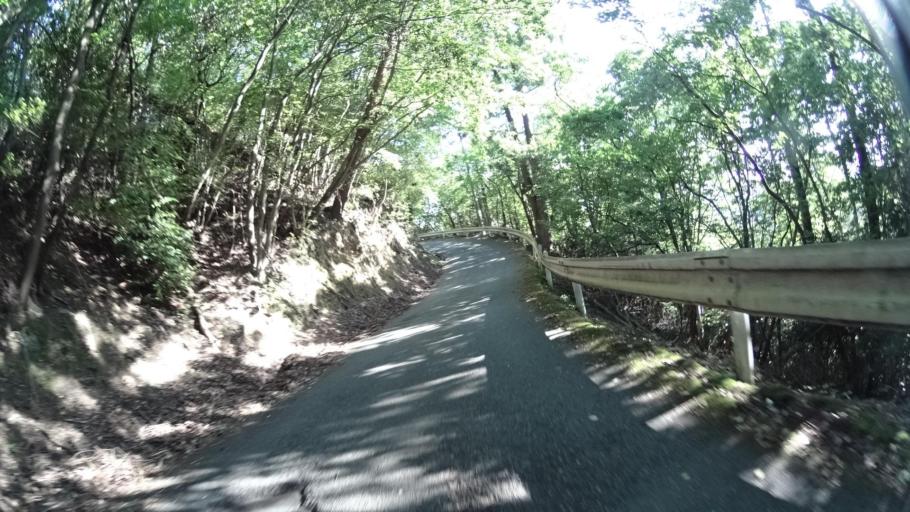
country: JP
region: Kyoto
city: Kameoka
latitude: 34.9818
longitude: 135.5566
